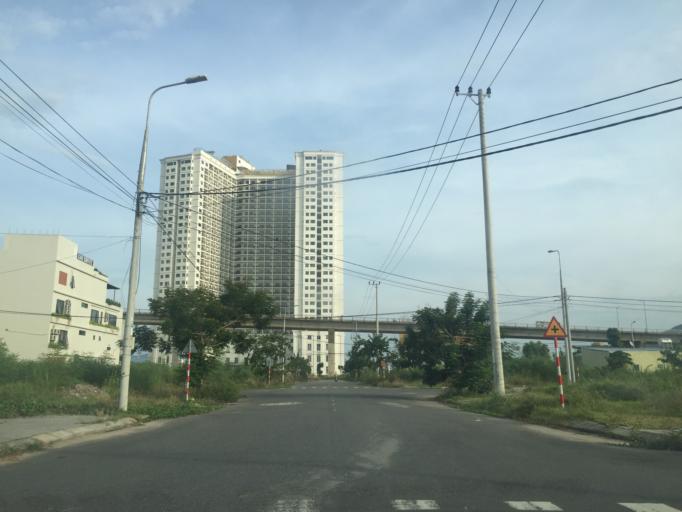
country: VN
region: Da Nang
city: Da Nang
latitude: 16.0959
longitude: 108.2261
